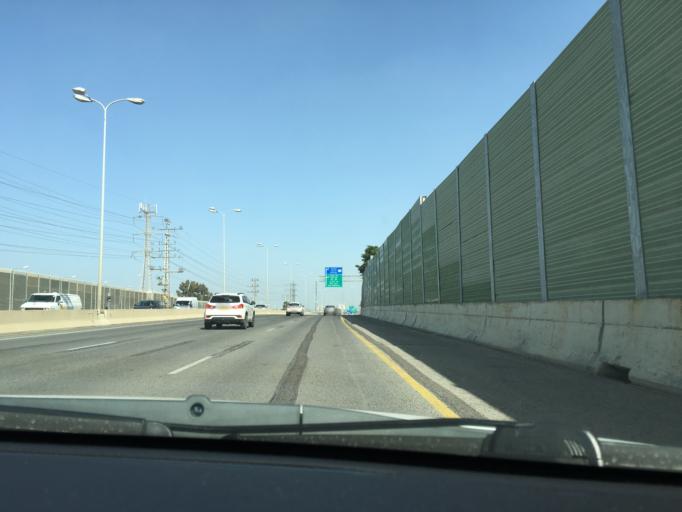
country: IL
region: Central District
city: Hod HaSharon
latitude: 32.1645
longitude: 34.8796
